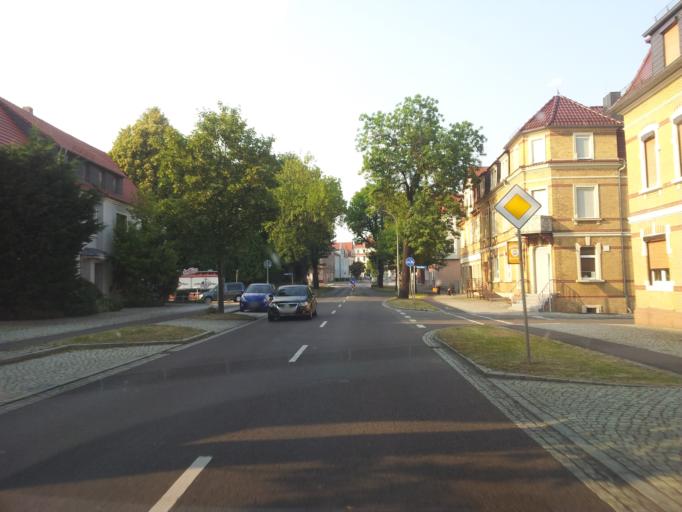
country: DE
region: Saxony
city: Bernsdorf
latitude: 51.3731
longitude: 14.0679
